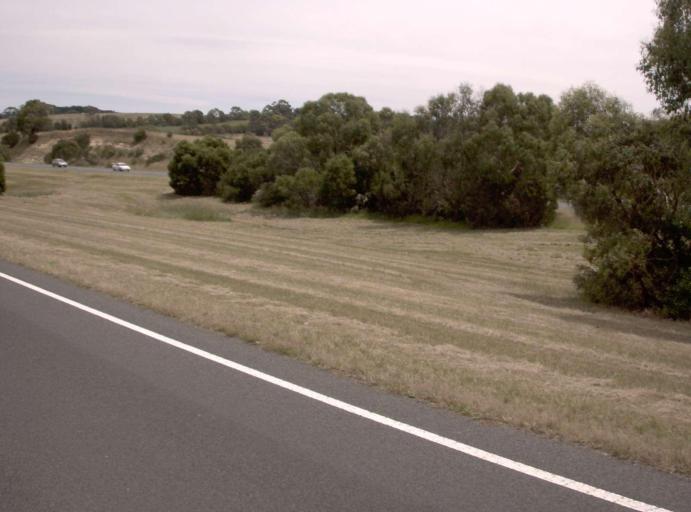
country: AU
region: Victoria
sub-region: Mornington Peninsula
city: Mount Martha
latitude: -38.2779
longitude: 145.0581
